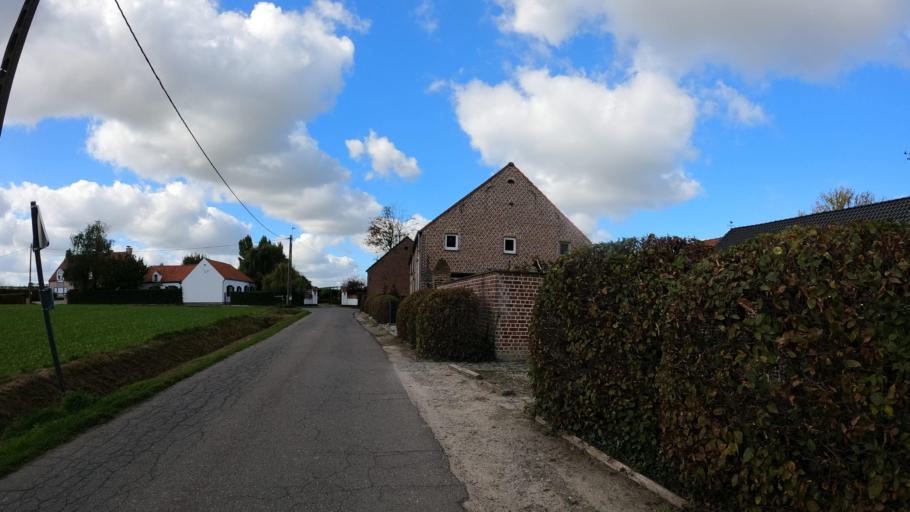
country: BE
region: Flanders
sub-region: Provincie Vlaams-Brabant
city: Opwijk
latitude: 50.9462
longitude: 4.2032
